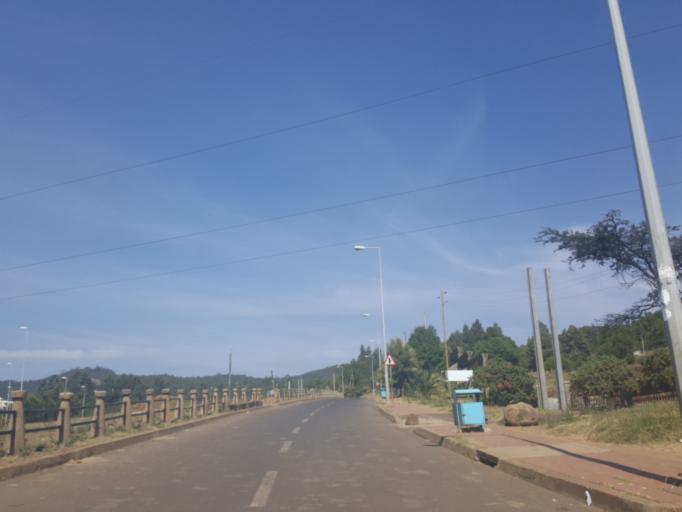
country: ET
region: Adis Abeba
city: Addis Ababa
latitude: 9.0690
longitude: 38.7237
